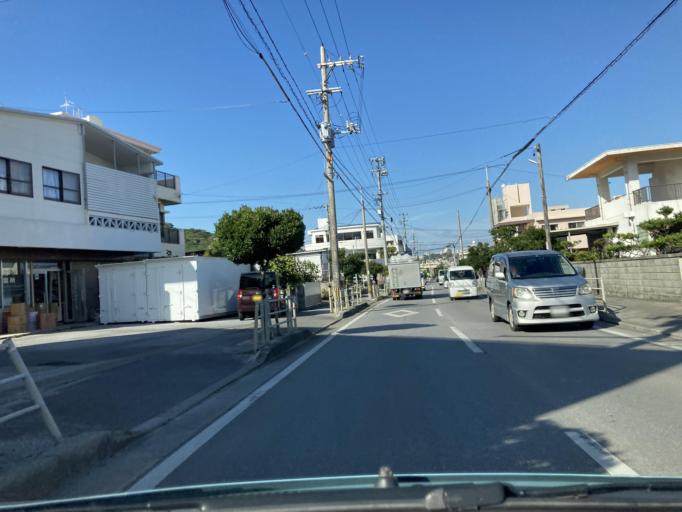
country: JP
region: Okinawa
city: Tomigusuku
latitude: 26.1810
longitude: 127.7068
